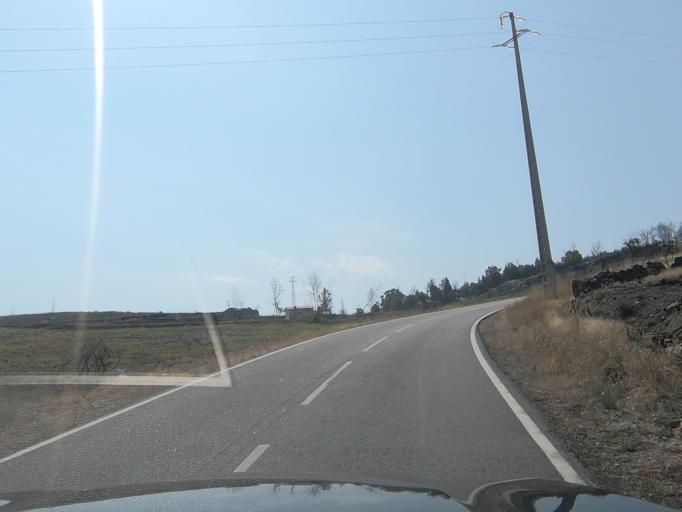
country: PT
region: Vila Real
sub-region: Sabrosa
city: Sabrosa
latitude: 41.3399
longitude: -7.5944
